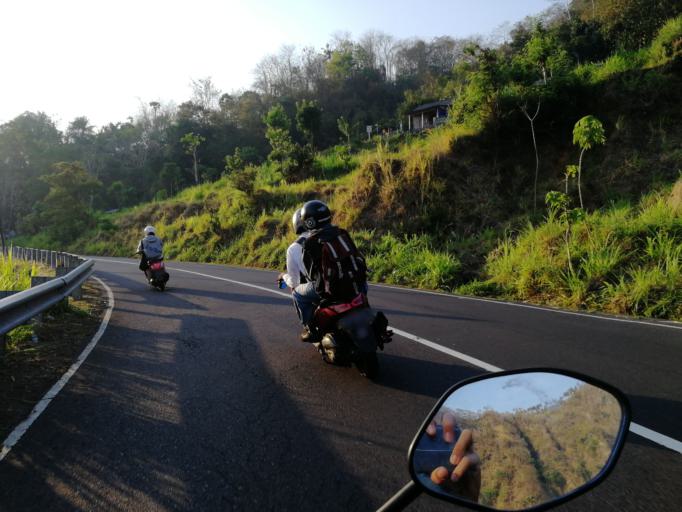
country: ID
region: Bali
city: Banjar Kangkaang
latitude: -8.3668
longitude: 115.6124
